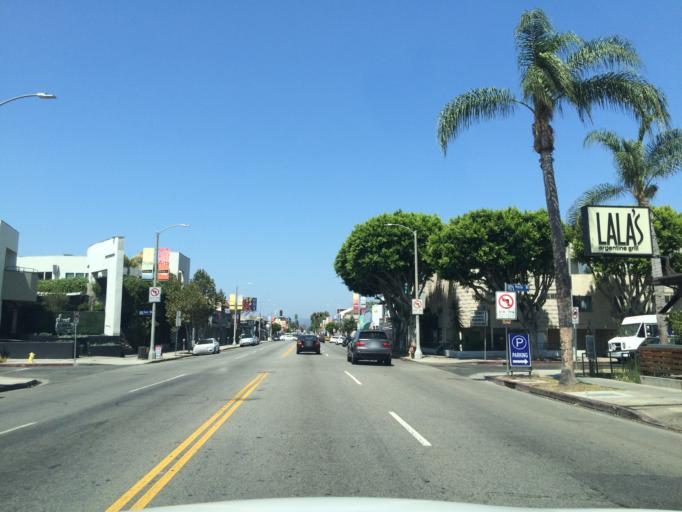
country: US
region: California
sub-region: Los Angeles County
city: West Hollywood
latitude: 34.0835
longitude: -118.3471
